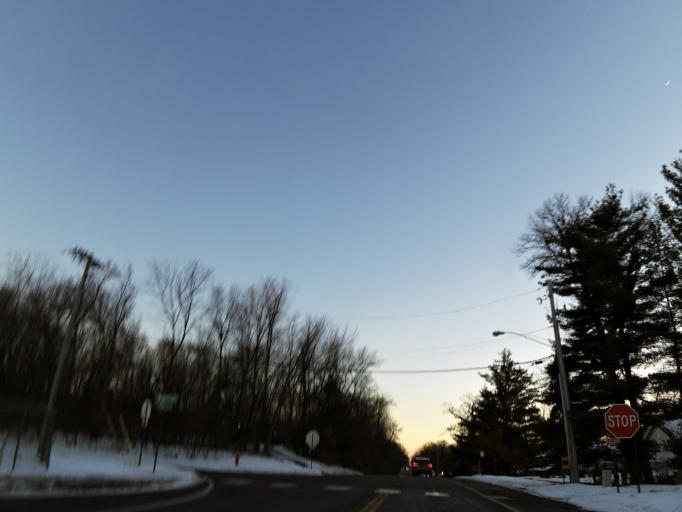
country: US
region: Minnesota
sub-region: Scott County
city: Savage
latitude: 44.8190
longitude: -93.3585
